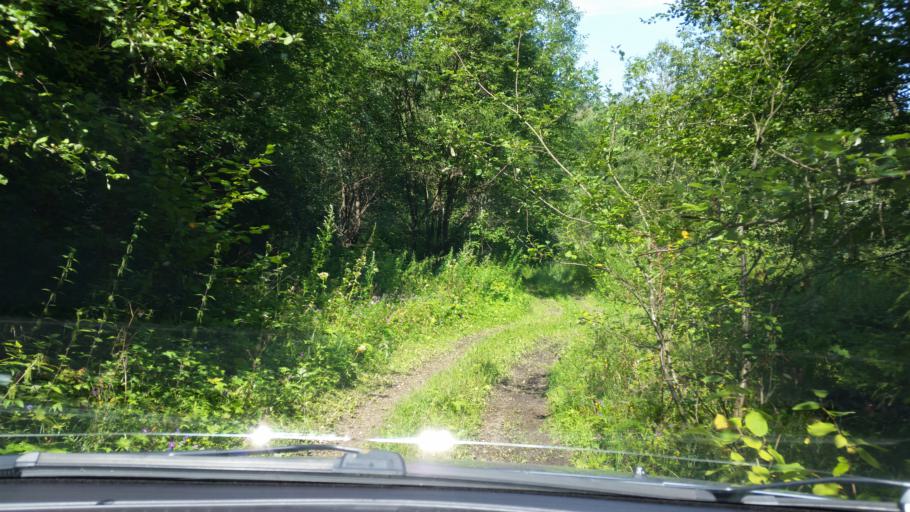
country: RU
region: Moskovskaya
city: Bol'shoye Gryzlovo
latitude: 54.9147
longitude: 37.7542
